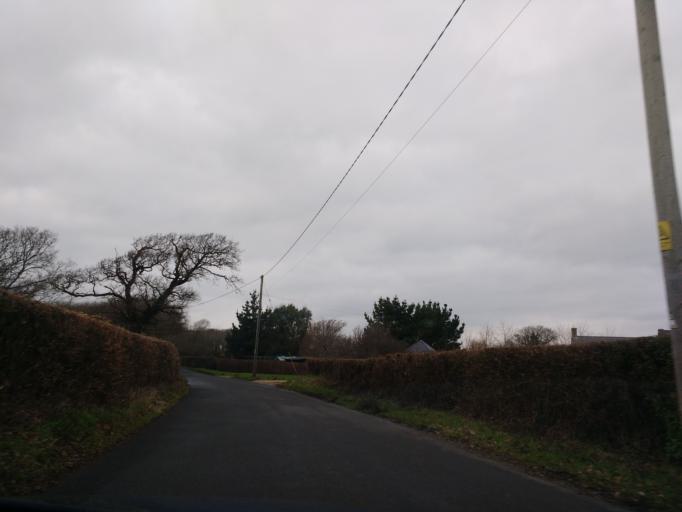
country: GB
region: England
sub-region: Isle of Wight
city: Shalfleet
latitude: 50.6935
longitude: -1.4024
